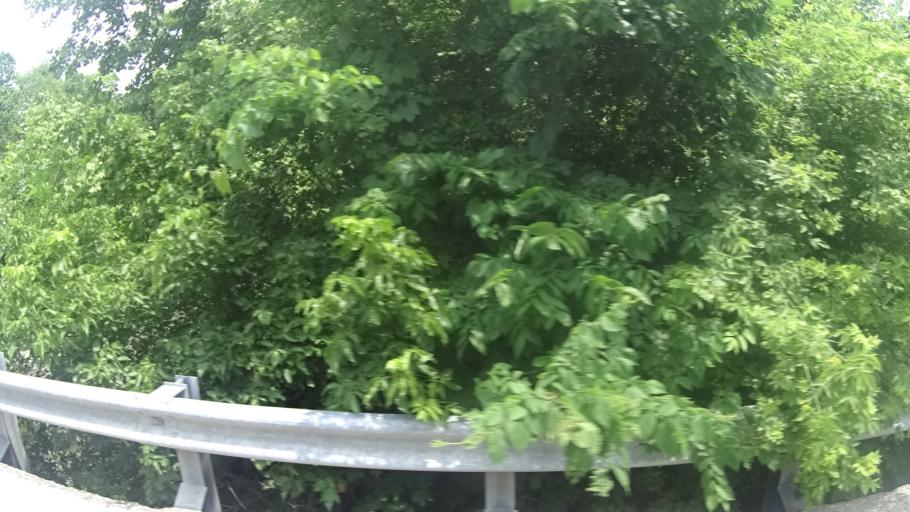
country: US
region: Ohio
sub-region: Erie County
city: Milan
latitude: 41.2864
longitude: -82.6426
